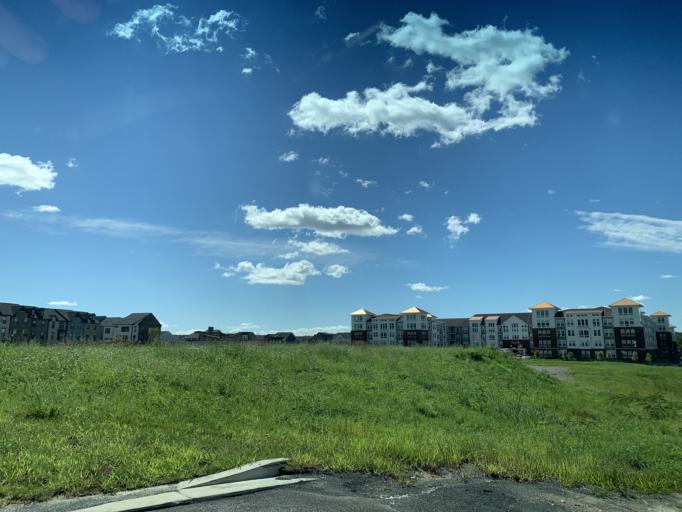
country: US
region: Maryland
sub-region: Baltimore County
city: Bowleys Quarters
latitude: 39.3621
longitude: -76.4041
